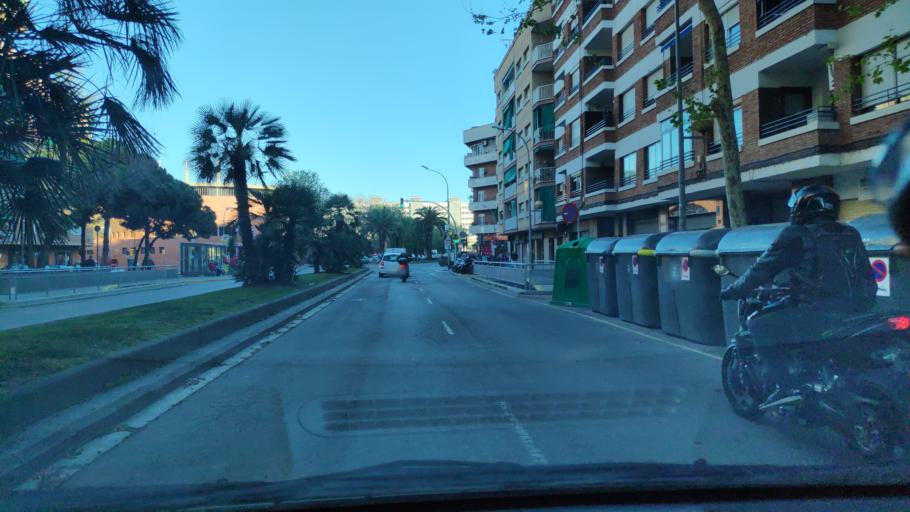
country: ES
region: Catalonia
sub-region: Provincia de Barcelona
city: Sant Adria de Besos
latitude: 41.4318
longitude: 2.2195
